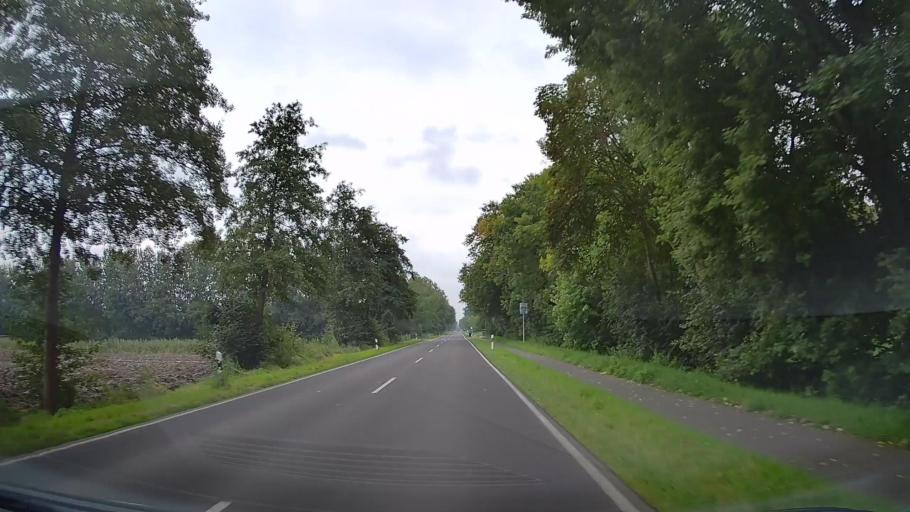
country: DE
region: Lower Saxony
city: Drochtersen
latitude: 53.7287
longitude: 9.3537
